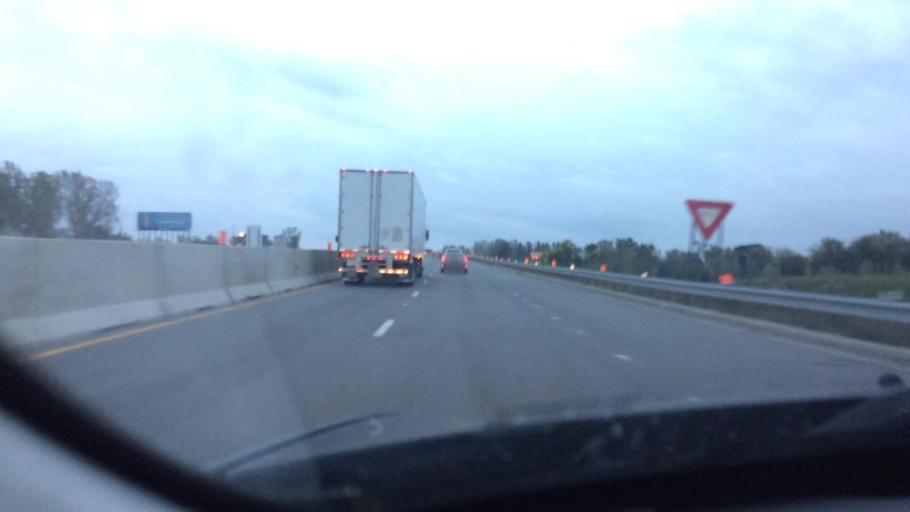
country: US
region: Ohio
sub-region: Hancock County
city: Findlay
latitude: 41.0552
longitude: -83.6705
